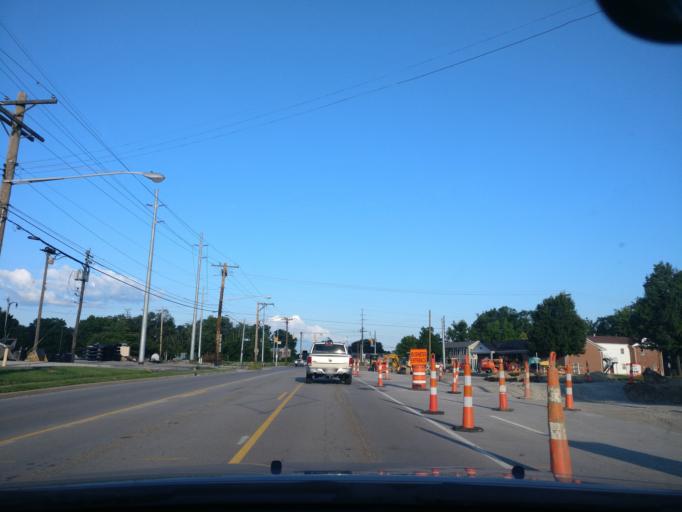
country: US
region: Ohio
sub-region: Warren County
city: Springboro
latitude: 39.5571
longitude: -84.2343
